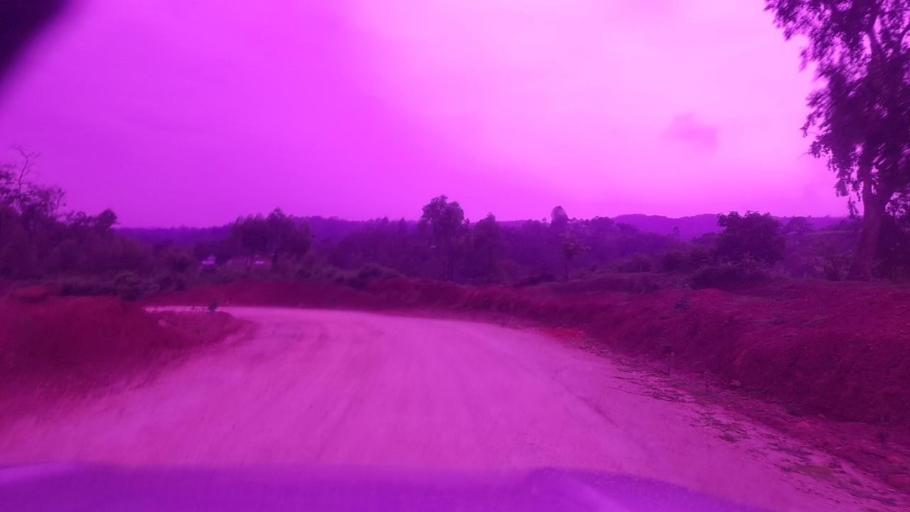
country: ET
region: Southern Nations, Nationalities, and People's Region
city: Bonga
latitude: 7.4517
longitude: 36.1355
